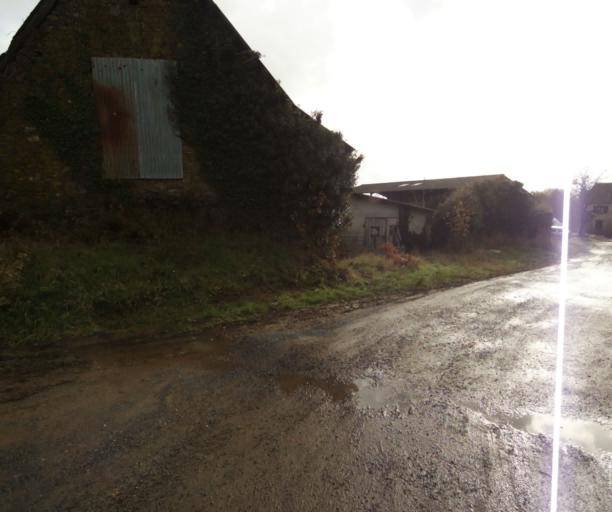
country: FR
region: Limousin
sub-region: Departement de la Correze
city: Sainte-Fereole
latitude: 45.2317
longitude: 1.6343
